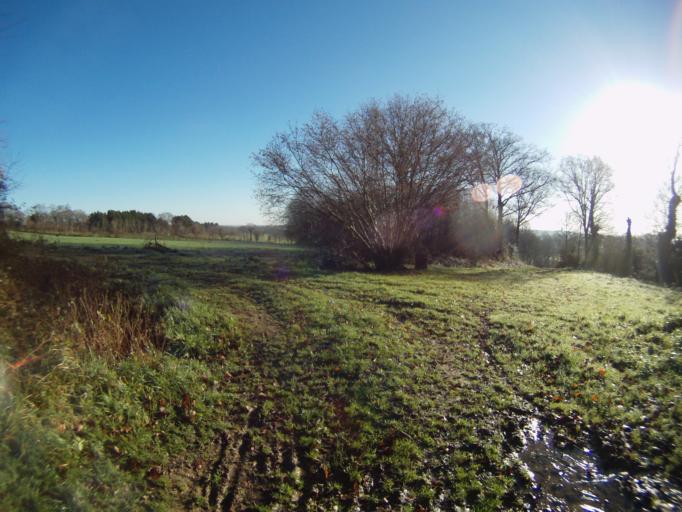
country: FR
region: Brittany
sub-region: Departement d'Ille-et-Vilaine
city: Chanteloup
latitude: 47.9364
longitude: -1.6218
